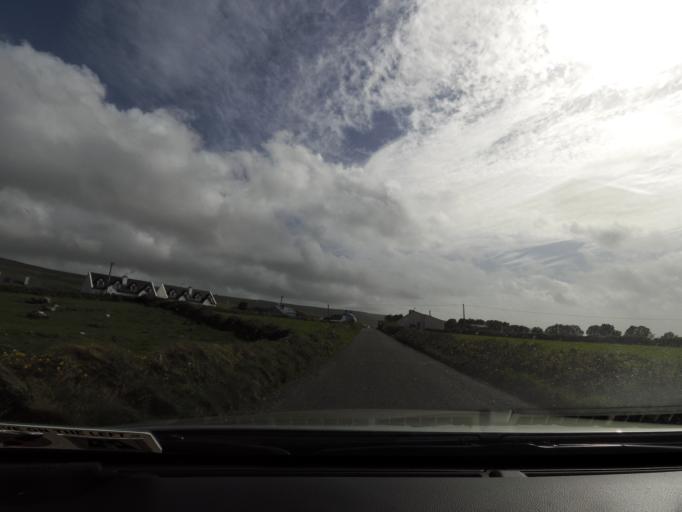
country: IE
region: Connaught
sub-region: County Galway
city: Bearna
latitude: 53.1033
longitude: -9.2962
